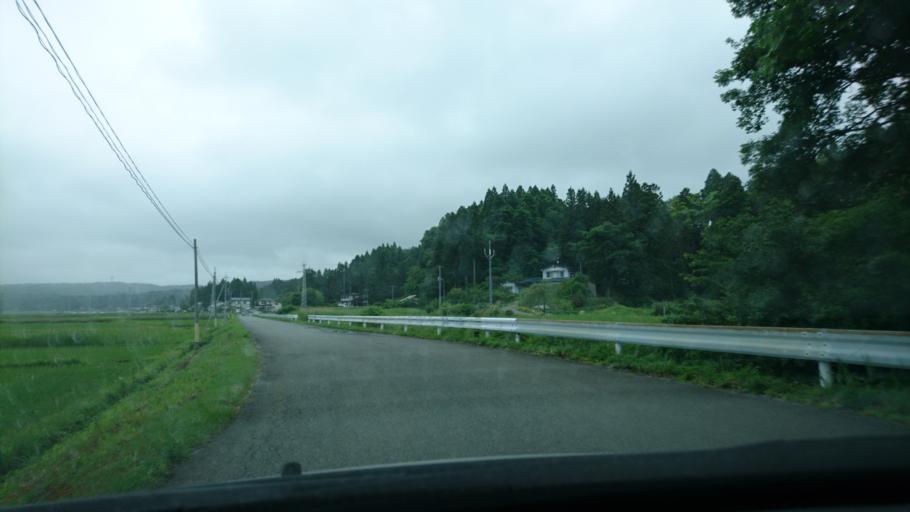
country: JP
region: Iwate
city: Ichinoseki
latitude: 38.9461
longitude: 141.0619
